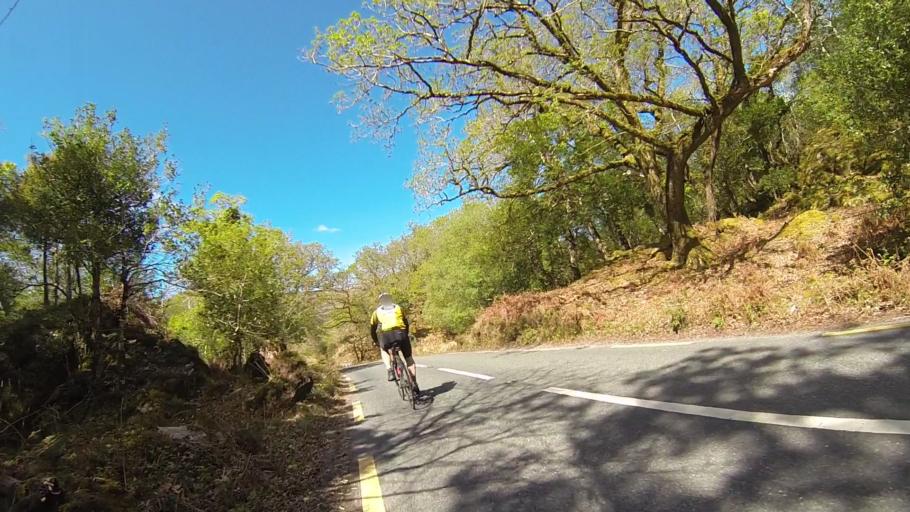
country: IE
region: Munster
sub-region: Ciarrai
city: Cill Airne
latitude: 51.9795
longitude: -9.5742
